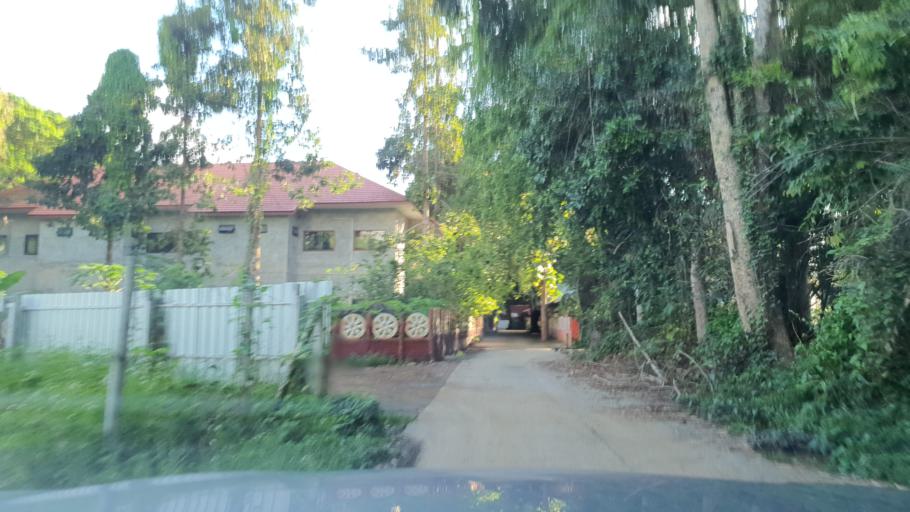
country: TH
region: Chiang Mai
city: San Sai
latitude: 18.8753
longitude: 99.1536
